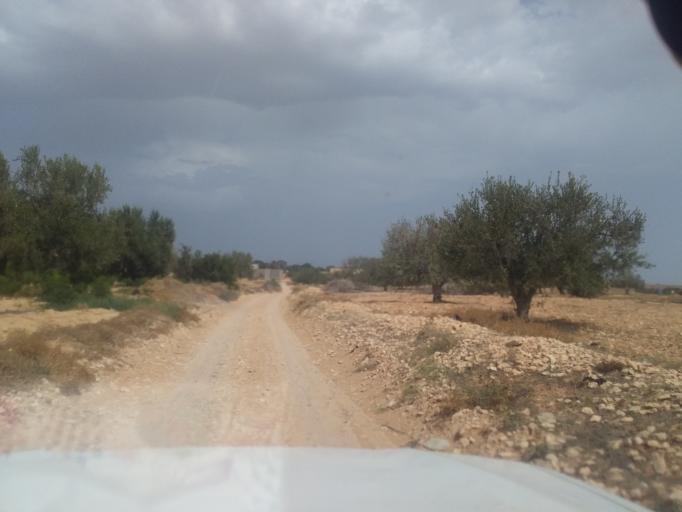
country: TN
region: Madanin
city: Medenine
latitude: 33.5892
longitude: 10.3245
